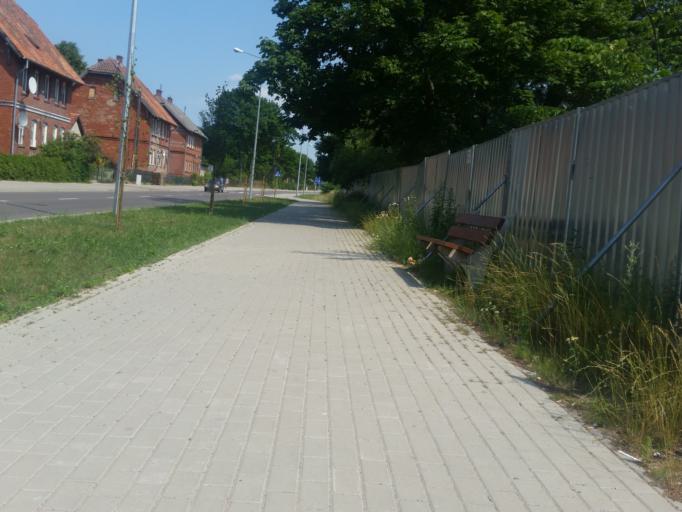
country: PL
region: Warmian-Masurian Voivodeship
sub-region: Powiat goldapski
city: Goldap
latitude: 54.3139
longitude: 22.3091
